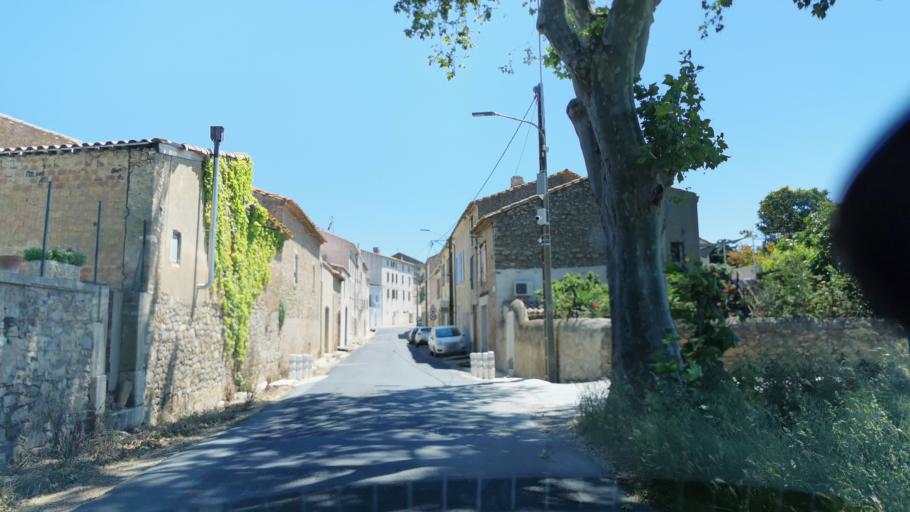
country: FR
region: Languedoc-Roussillon
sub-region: Departement de l'Aude
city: Saint-Marcel-sur-Aude
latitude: 43.2431
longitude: 2.9203
